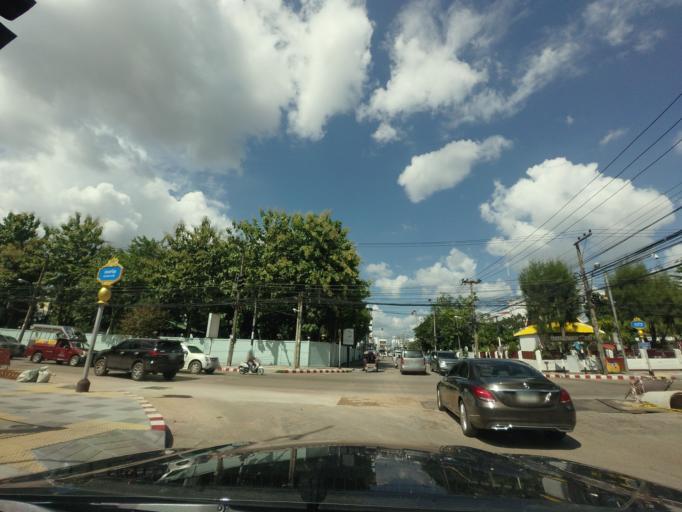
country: TH
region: Changwat Udon Thani
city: Udon Thani
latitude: 17.4049
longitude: 102.7866
